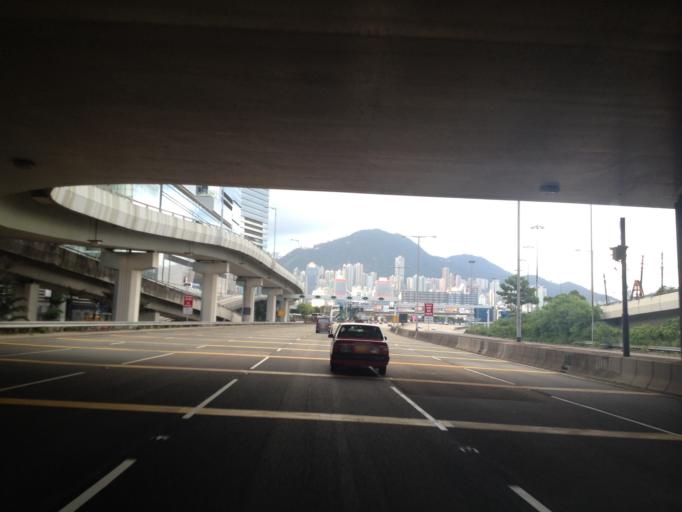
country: HK
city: Hong Kong
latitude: 22.3077
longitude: 114.1611
